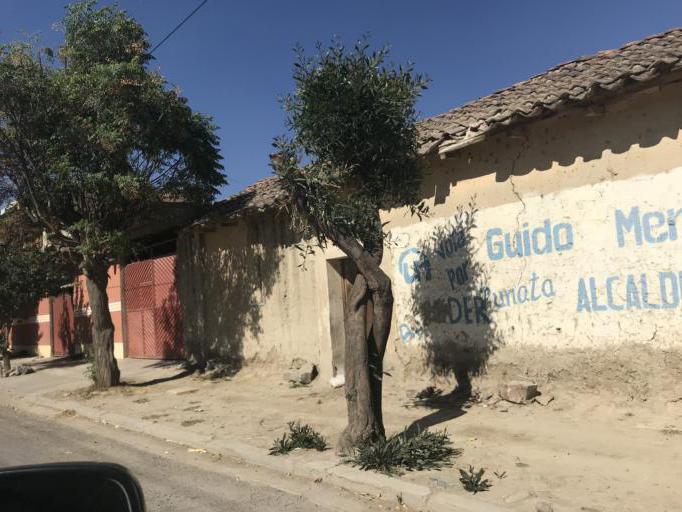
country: BO
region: Cochabamba
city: Punata
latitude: -17.5502
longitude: -65.8474
